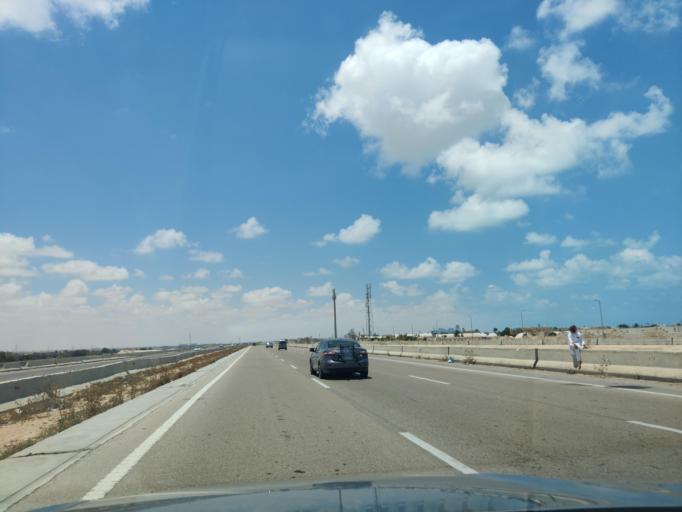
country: EG
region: Muhafazat Matruh
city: Al `Alamayn
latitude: 30.8139
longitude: 29.0466
